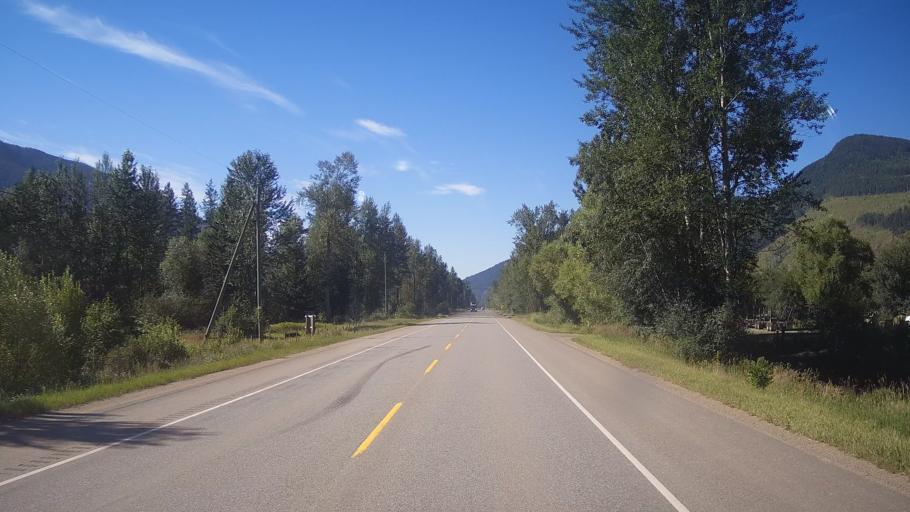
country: CA
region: British Columbia
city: Chase
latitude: 51.5236
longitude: -120.1715
